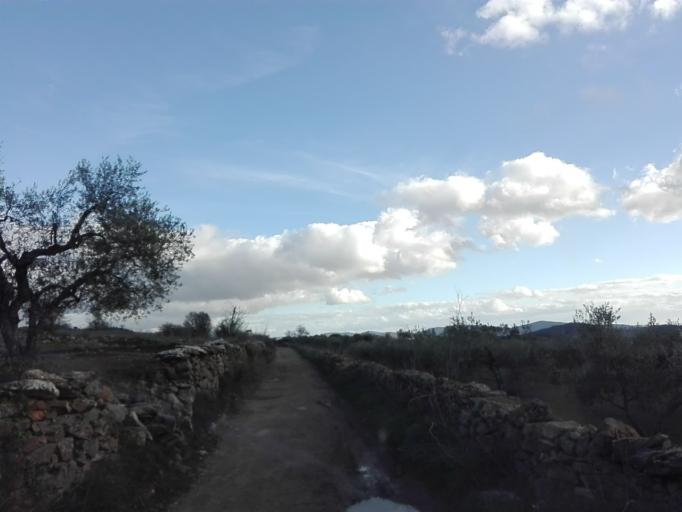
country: ES
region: Extremadura
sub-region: Provincia de Badajoz
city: Trasierra
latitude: 38.1867
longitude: -5.9889
